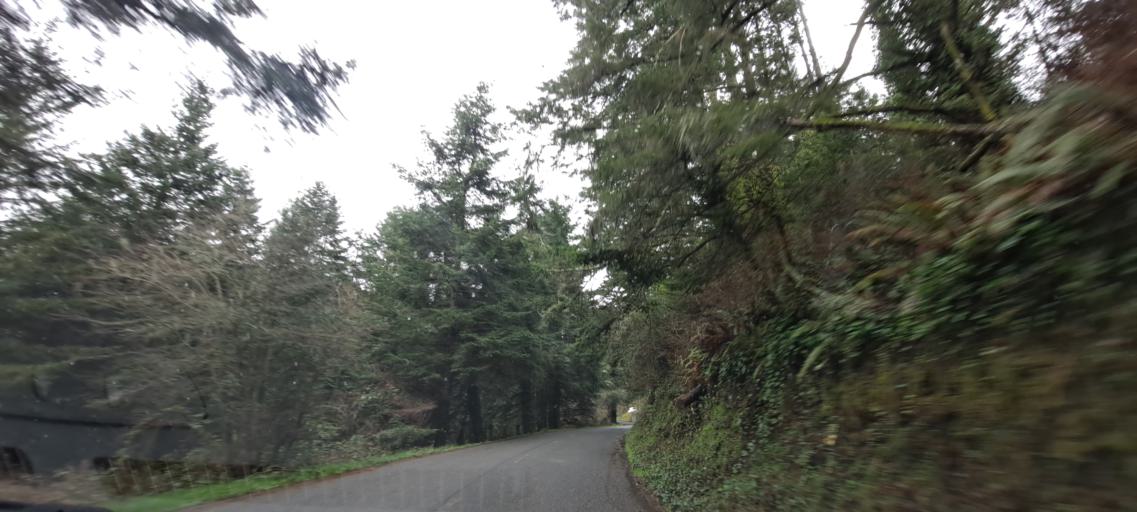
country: US
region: California
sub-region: Humboldt County
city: Fortuna
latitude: 40.5973
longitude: -124.1424
